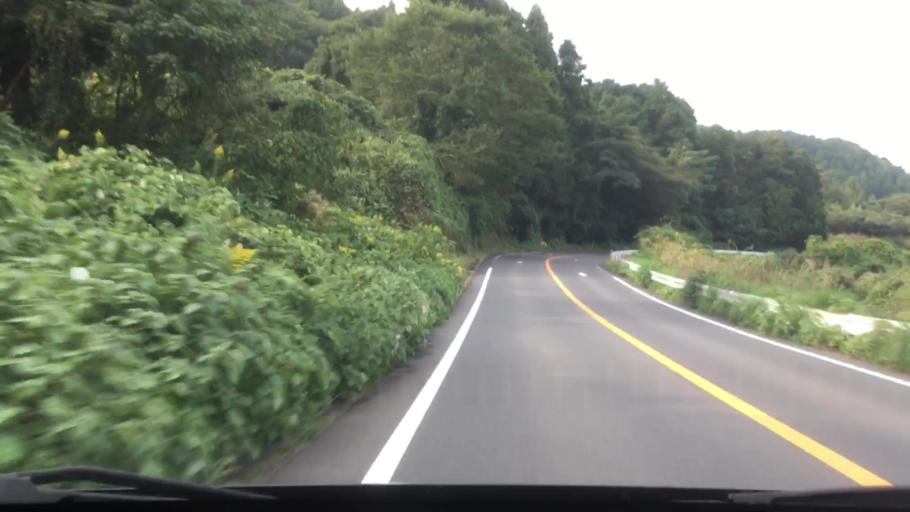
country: JP
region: Nagasaki
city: Sasebo
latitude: 33.0394
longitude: 129.6882
